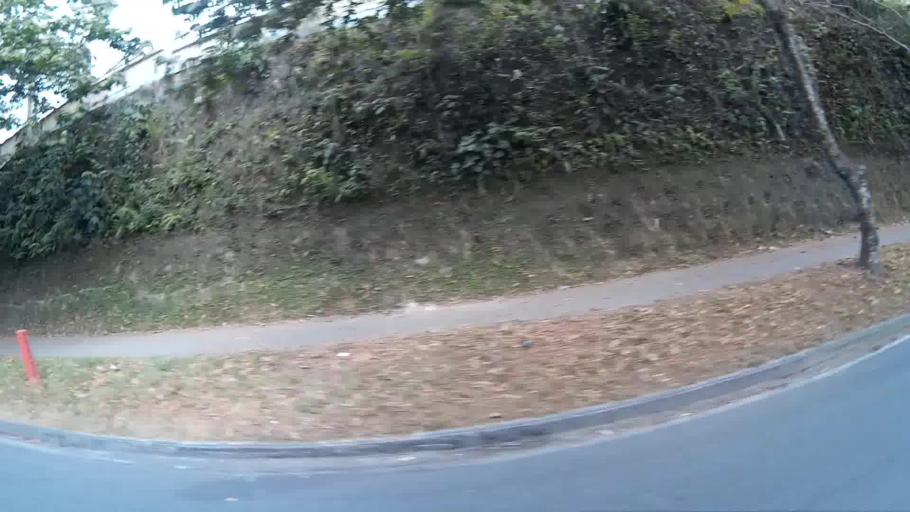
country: CO
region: Quindio
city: Armenia
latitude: 4.5432
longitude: -75.6602
